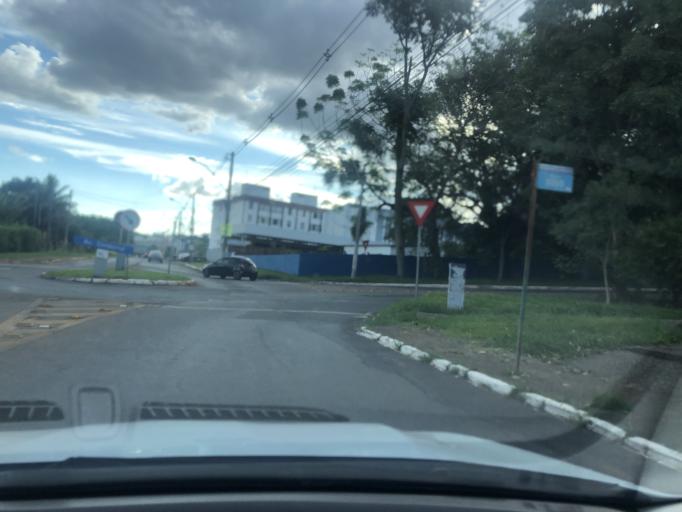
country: BR
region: Federal District
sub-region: Brasilia
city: Brasilia
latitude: -15.8744
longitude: -47.9715
